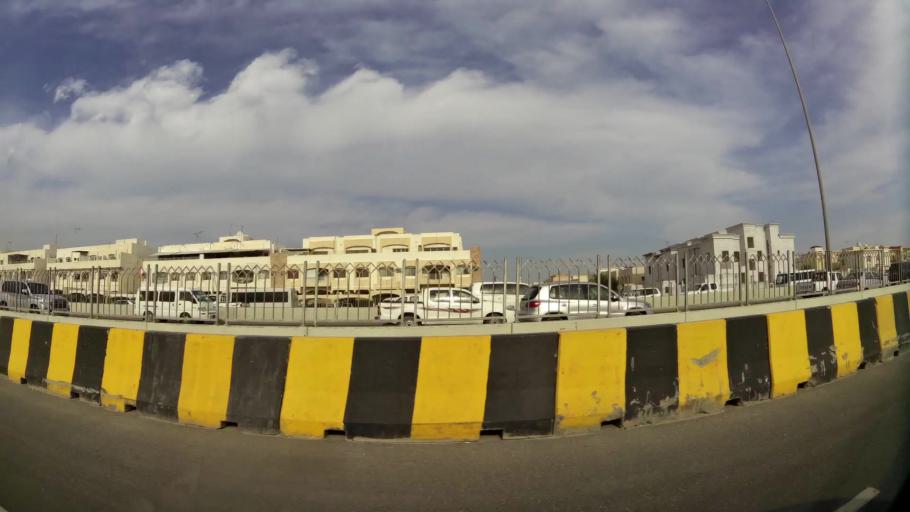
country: QA
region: Baladiyat ar Rayyan
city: Ar Rayyan
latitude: 25.3102
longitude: 51.4719
